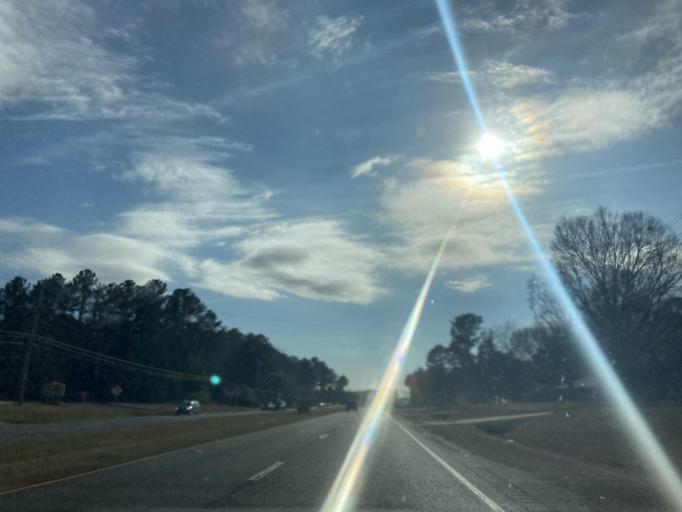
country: US
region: Georgia
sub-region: Jones County
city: Gray
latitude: 33.0022
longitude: -83.5505
